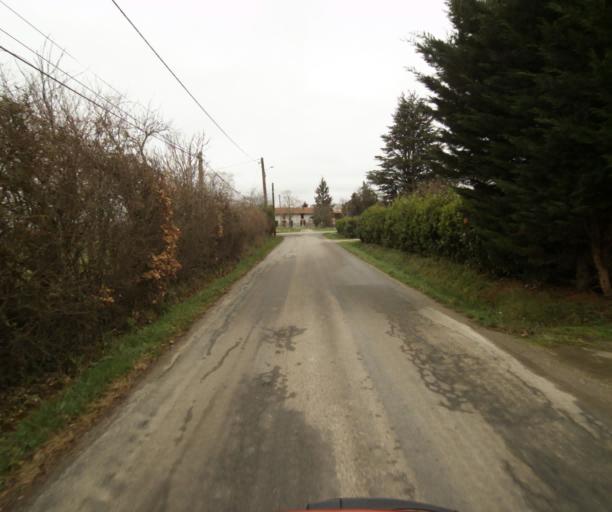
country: FR
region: Midi-Pyrenees
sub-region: Departement de l'Ariege
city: Saverdun
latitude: 43.2601
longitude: 1.5299
